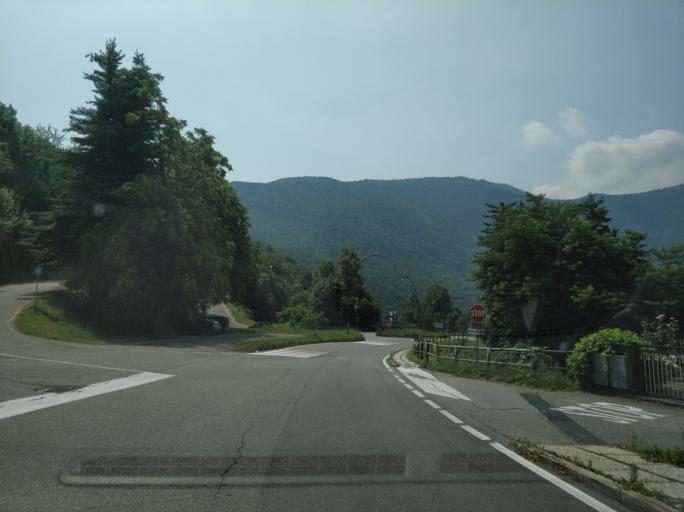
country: IT
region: Piedmont
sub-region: Provincia di Torino
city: Lanzo Torinese
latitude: 45.2709
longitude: 7.4772
